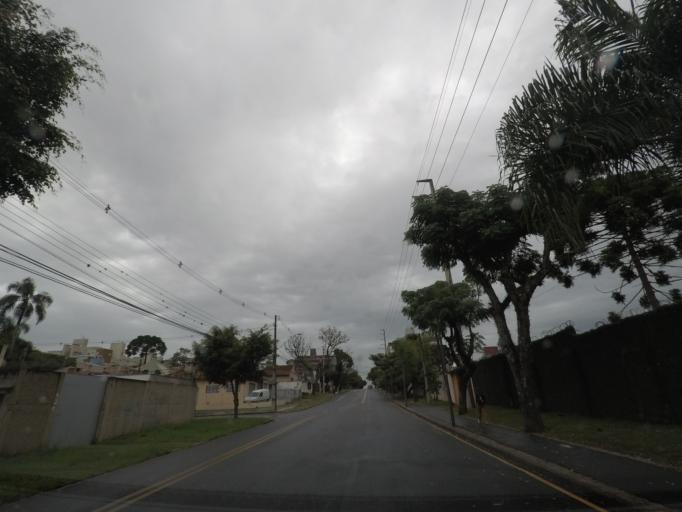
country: BR
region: Parana
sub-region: Curitiba
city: Curitiba
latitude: -25.4567
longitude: -49.2822
